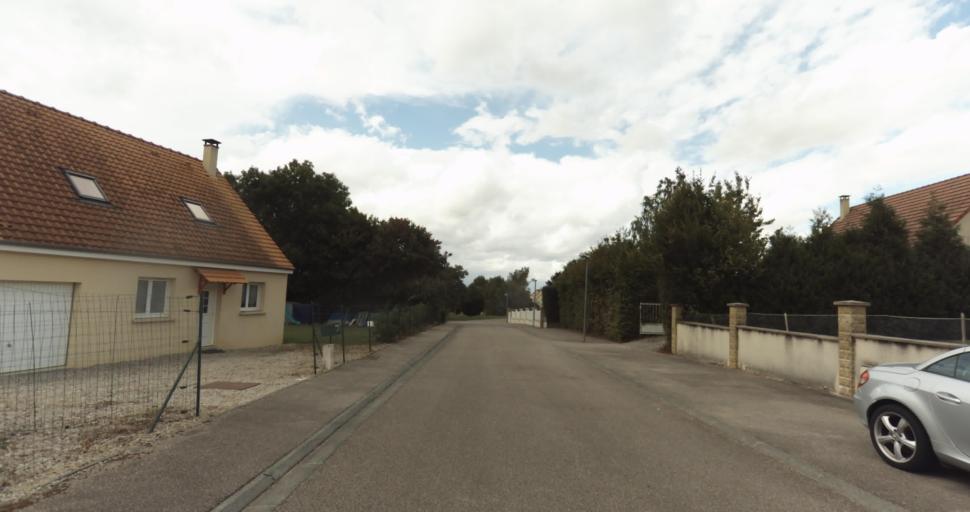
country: FR
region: Lower Normandy
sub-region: Departement de l'Orne
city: Gace
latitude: 48.7854
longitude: 0.3010
